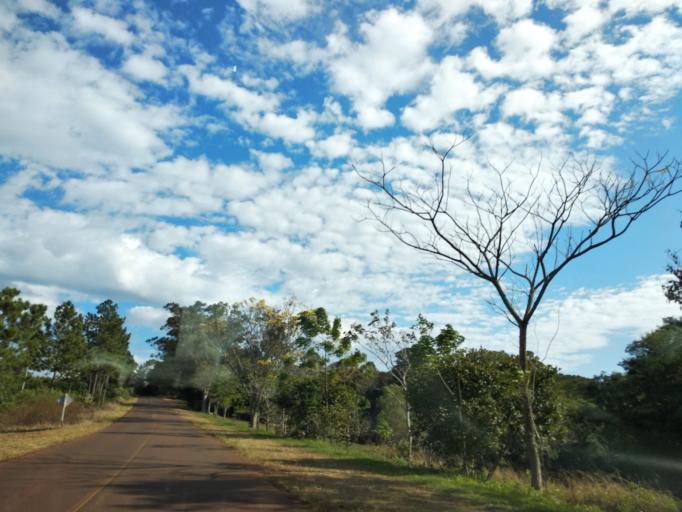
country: AR
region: Misiones
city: Aristobulo del Valle
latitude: -27.0720
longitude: -54.8306
